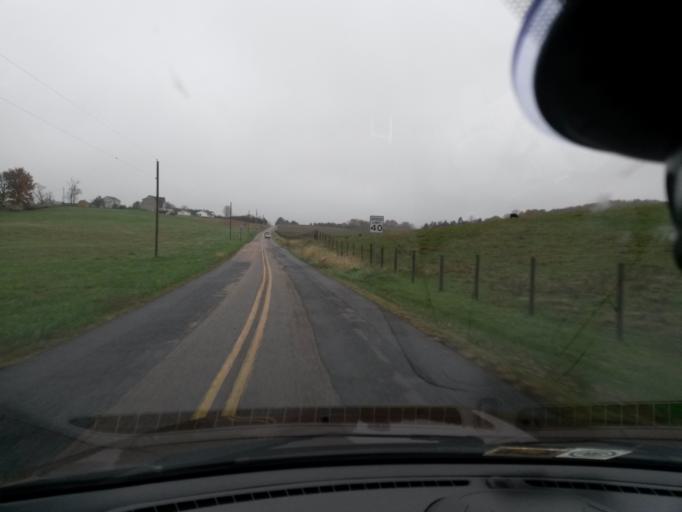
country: US
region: Virginia
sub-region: Botetourt County
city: Fincastle
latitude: 37.4759
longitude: -79.8555
